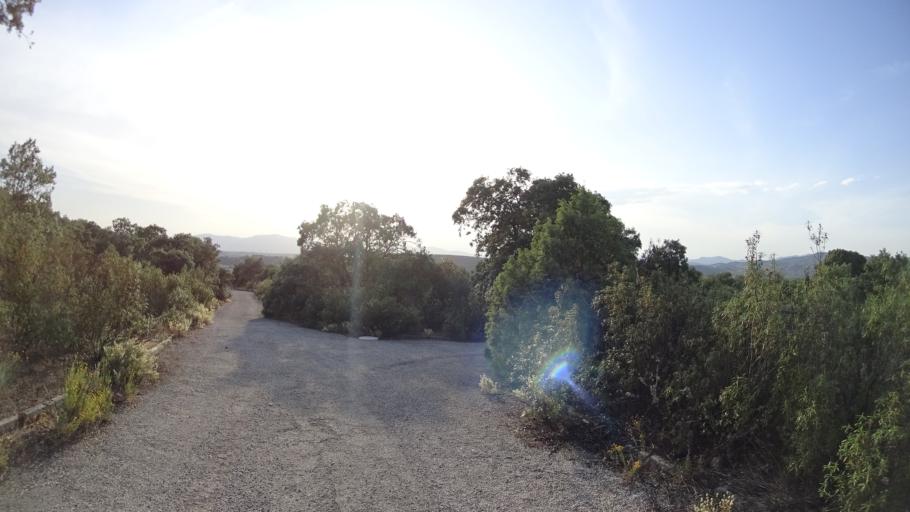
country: ES
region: Madrid
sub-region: Provincia de Madrid
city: Torrelodones
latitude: 40.5941
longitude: -3.9420
